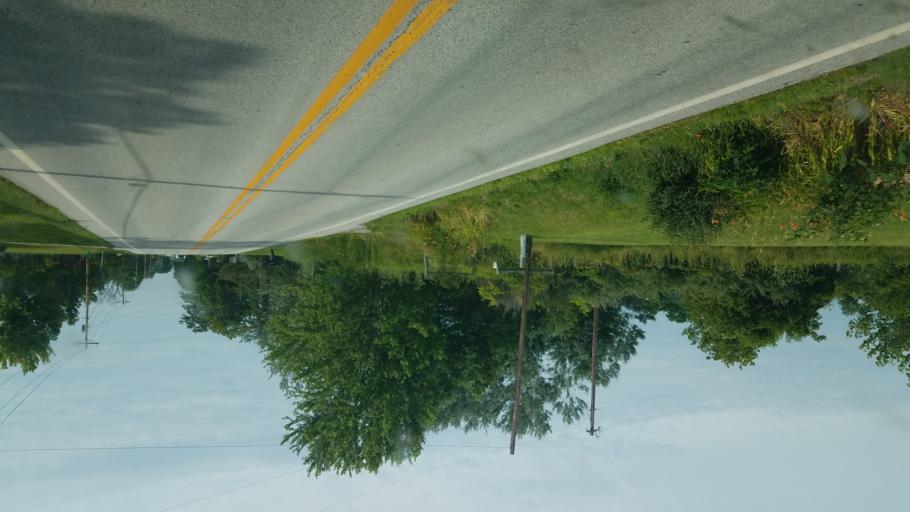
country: US
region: Ohio
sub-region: Medina County
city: Lodi
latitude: 41.0700
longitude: -82.0245
